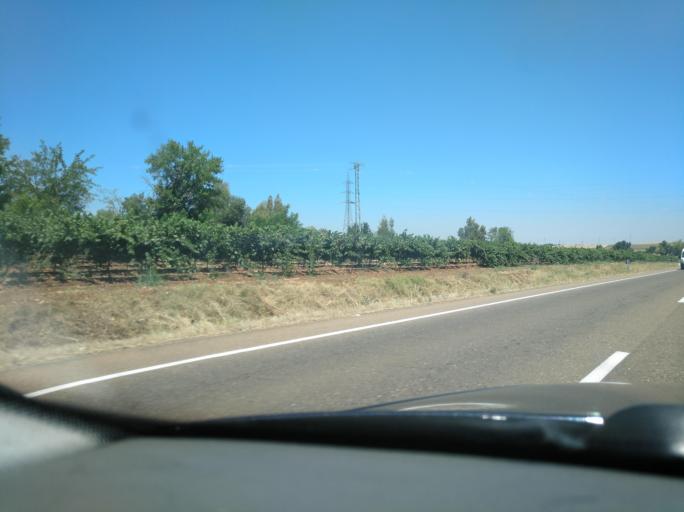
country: ES
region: Extremadura
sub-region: Provincia de Badajoz
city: Olivenza
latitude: 38.7362
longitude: -7.0675
